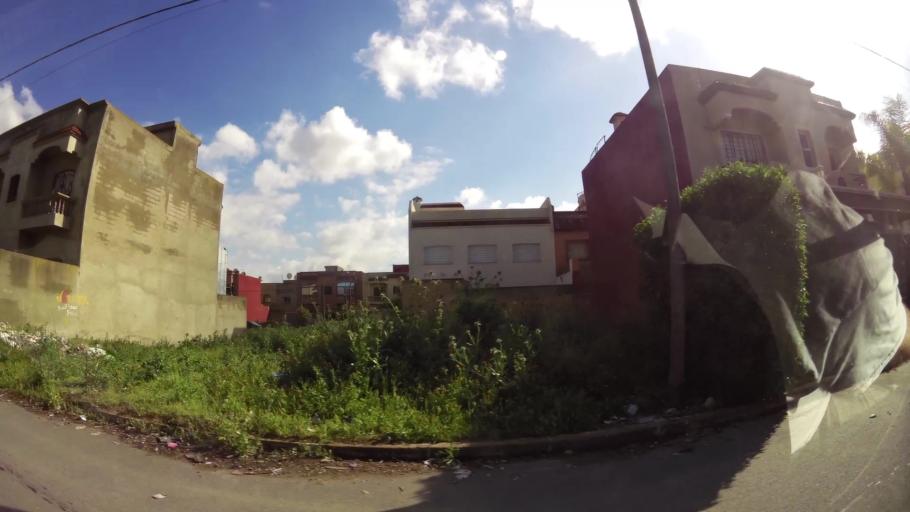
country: MA
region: Grand Casablanca
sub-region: Mediouna
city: Mediouna
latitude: 33.3848
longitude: -7.5365
